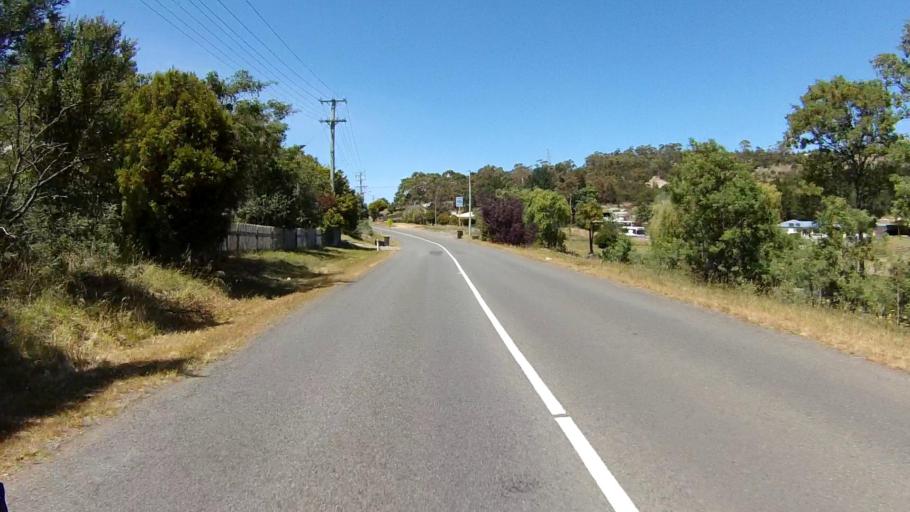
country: AU
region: Tasmania
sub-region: Clarence
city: Howrah
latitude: -42.8579
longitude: 147.4139
